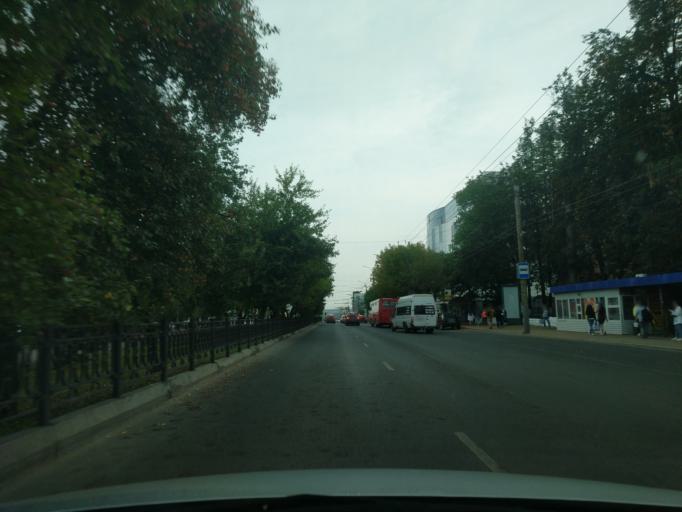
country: RU
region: Kirov
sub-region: Kirovo-Chepetskiy Rayon
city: Kirov
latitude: 58.5953
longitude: 49.6578
